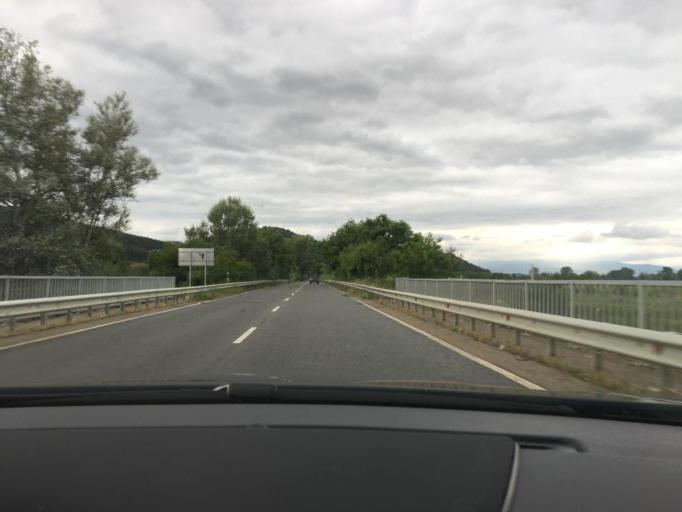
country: BG
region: Kyustendil
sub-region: Obshtina Kyustendil
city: Kyustendil
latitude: 42.2576
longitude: 22.8500
